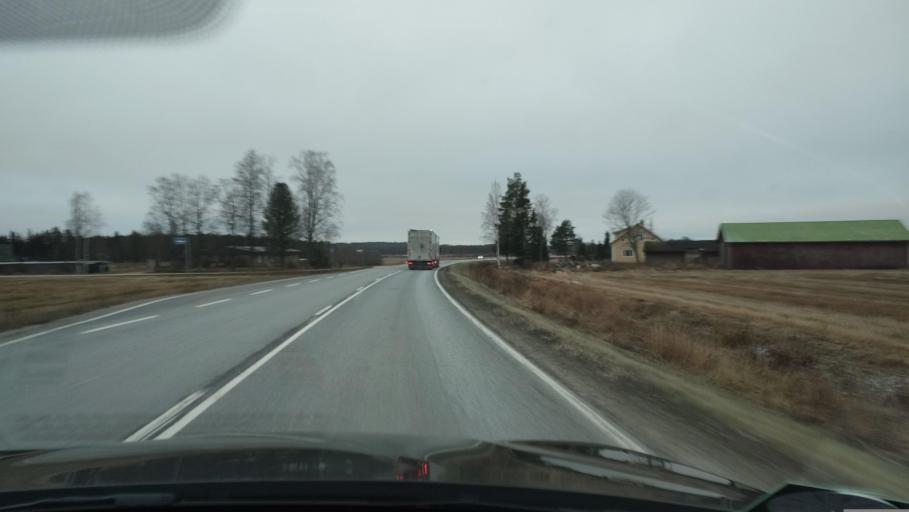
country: FI
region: Southern Ostrobothnia
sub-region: Suupohja
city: Kauhajoki
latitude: 62.3848
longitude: 22.1377
